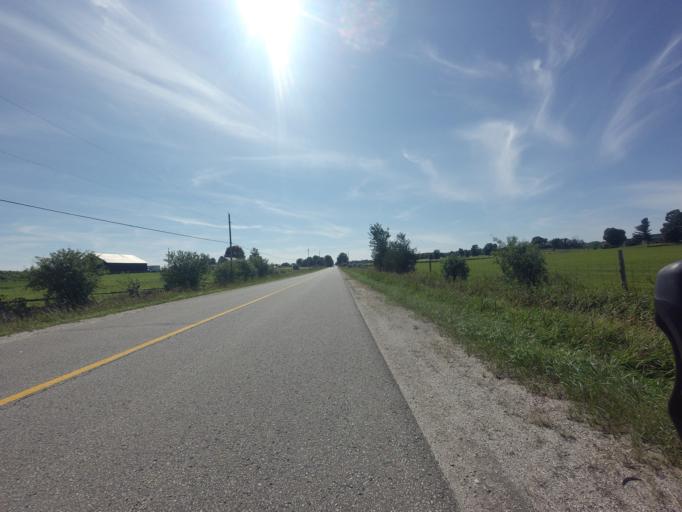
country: CA
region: Ontario
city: Perth
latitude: 44.9637
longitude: -76.2827
